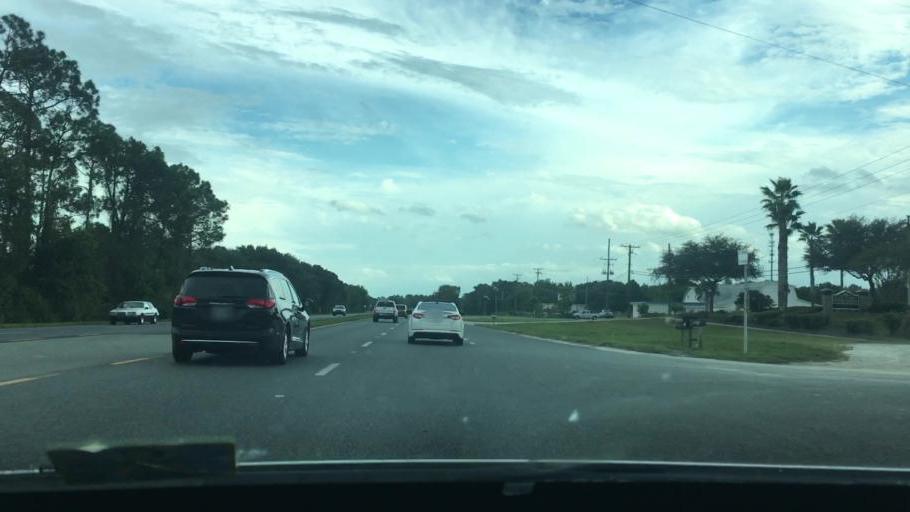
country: US
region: Florida
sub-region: Orange County
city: Bithlo
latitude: 28.5436
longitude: -81.0884
